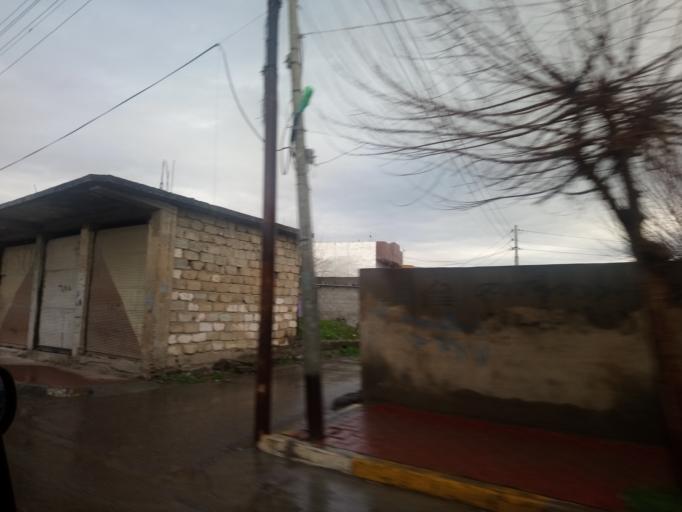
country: IQ
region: As Sulaymaniyah
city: Qeladize
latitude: 36.1845
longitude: 45.1201
